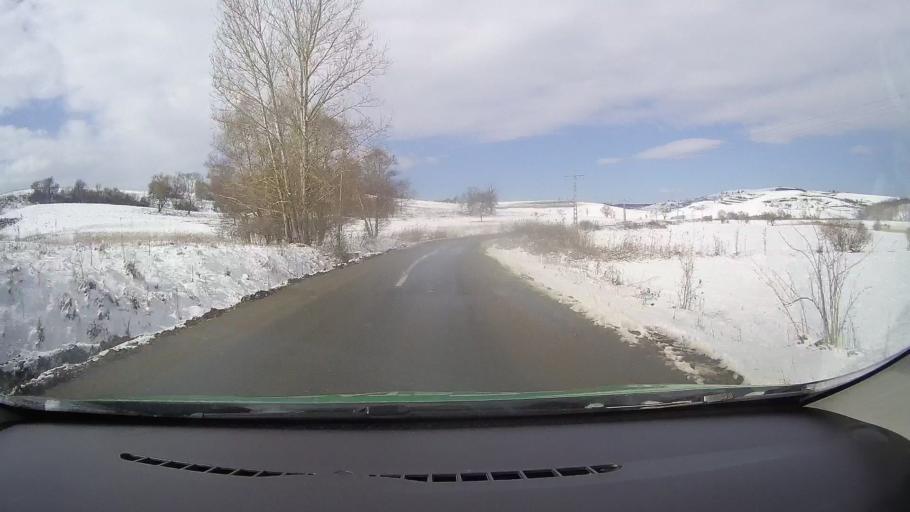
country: RO
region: Sibiu
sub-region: Comuna Altina
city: Altina
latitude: 45.9703
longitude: 24.4679
